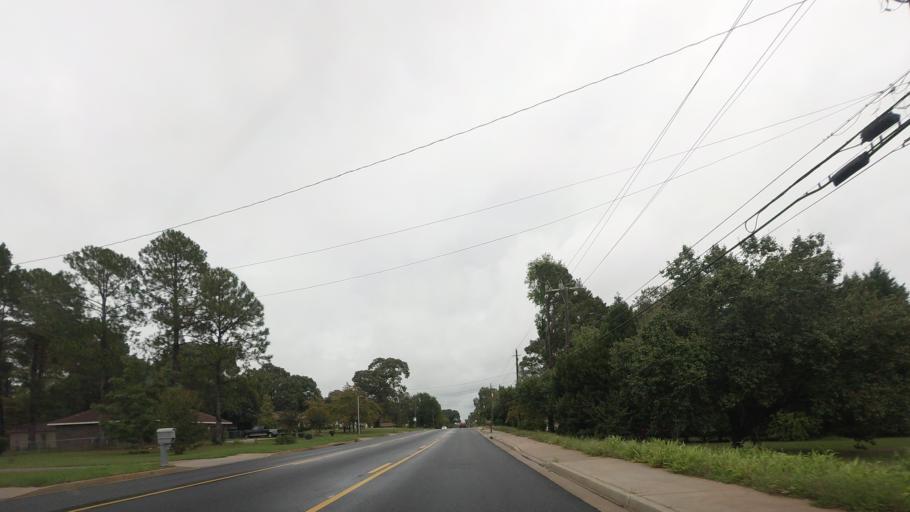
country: US
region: Georgia
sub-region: Houston County
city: Warner Robins
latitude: 32.5747
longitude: -83.6391
